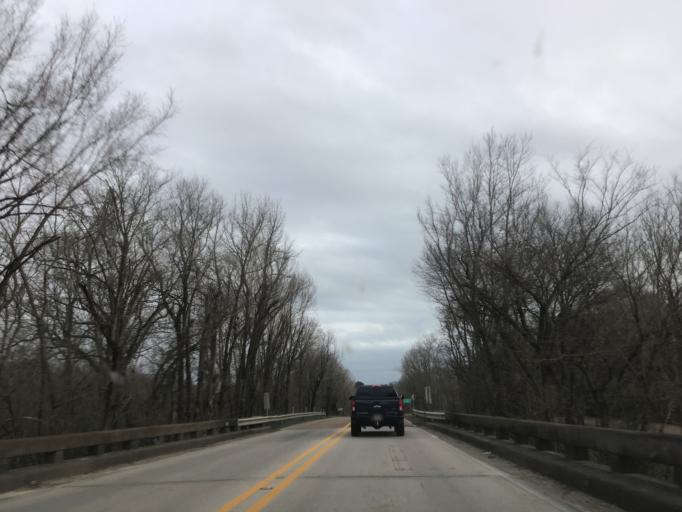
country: US
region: Mississippi
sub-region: Warren County
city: Beechwood
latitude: 32.3268
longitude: -90.8173
